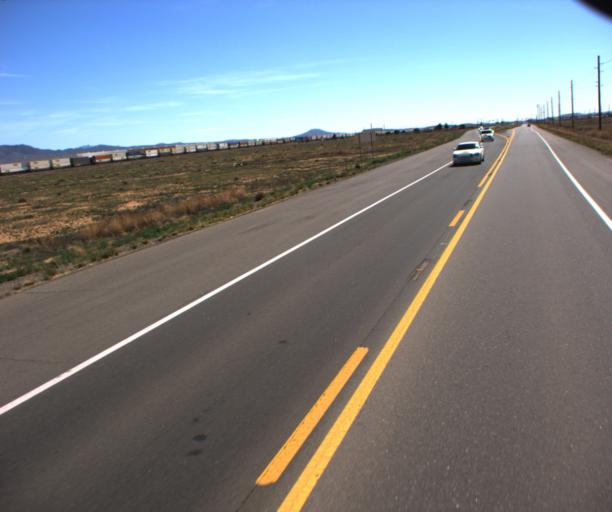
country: US
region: Arizona
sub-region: Mohave County
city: New Kingman-Butler
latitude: 35.2759
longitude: -113.9547
